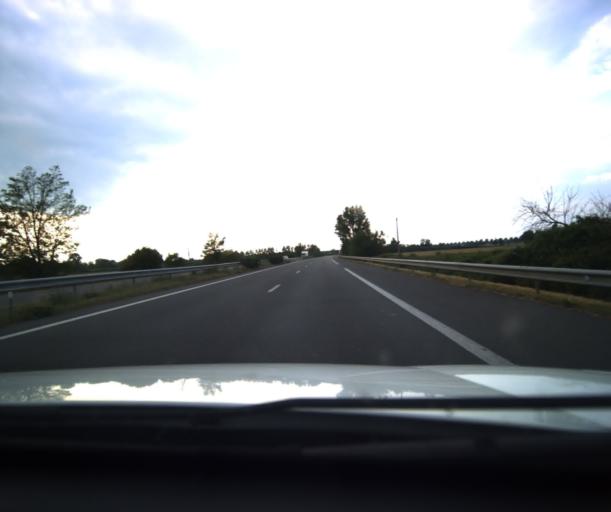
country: FR
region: Midi-Pyrenees
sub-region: Departement du Tarn-et-Garonne
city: Saint-Porquier
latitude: 44.0225
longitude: 1.1739
